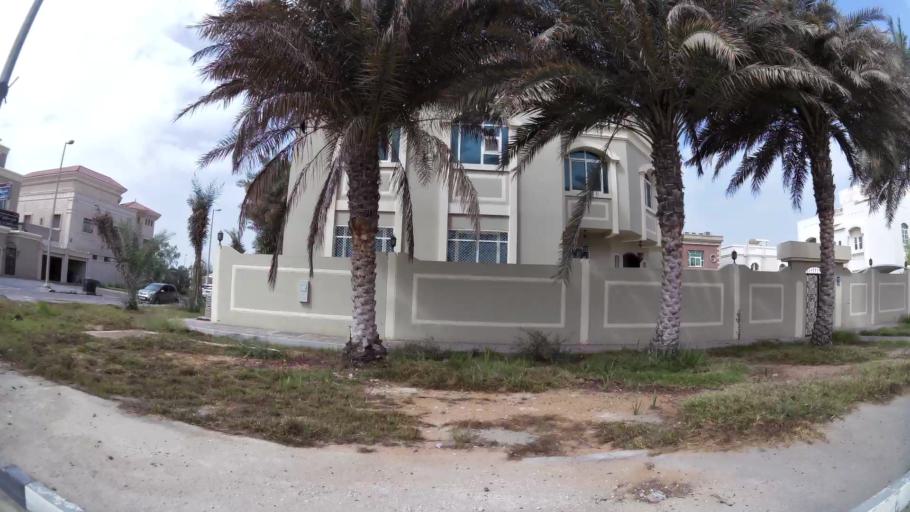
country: AE
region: Abu Dhabi
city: Abu Dhabi
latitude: 24.3948
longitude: 54.4940
